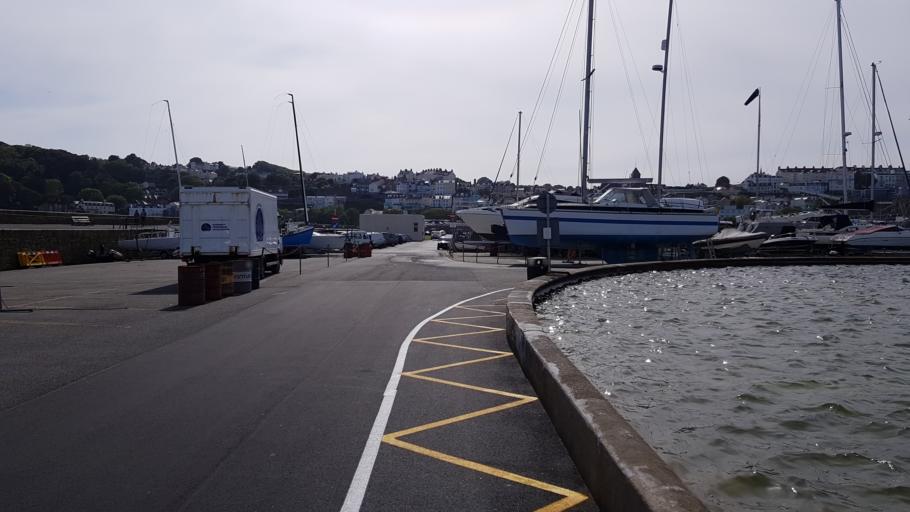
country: GG
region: St Peter Port
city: Saint Peter Port
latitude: 49.4534
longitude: -2.5299
